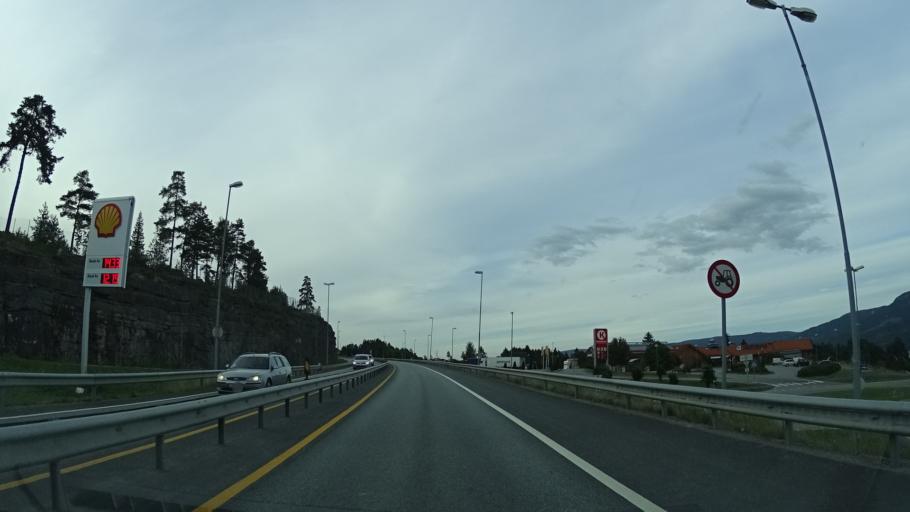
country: NO
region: Buskerud
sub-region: Hole
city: Vik
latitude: 60.0814
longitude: 10.2857
